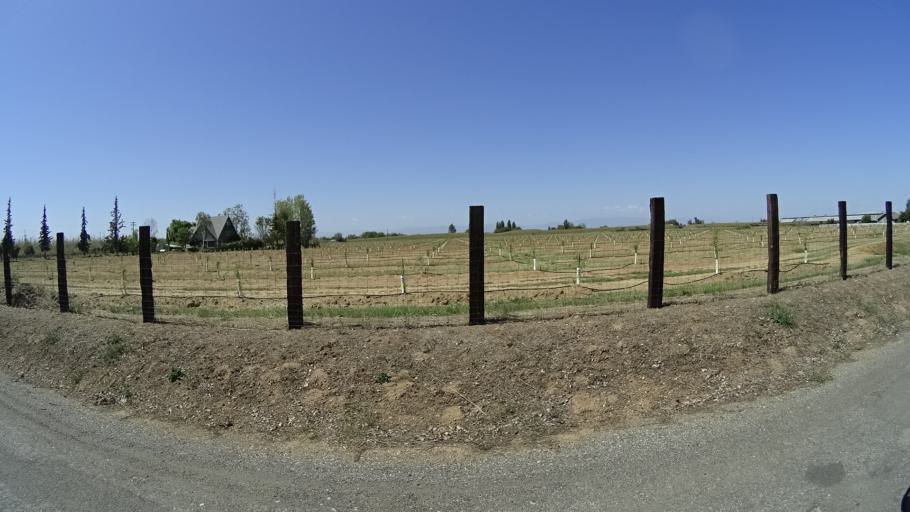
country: US
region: California
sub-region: Glenn County
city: Orland
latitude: 39.7712
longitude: -122.1502
